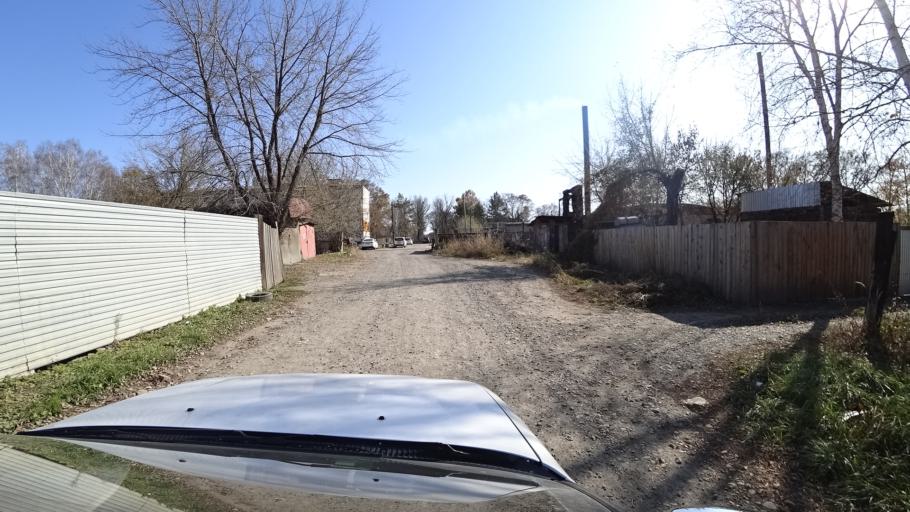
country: RU
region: Primorskiy
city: Dal'nerechensk
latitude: 45.9338
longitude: 133.7229
